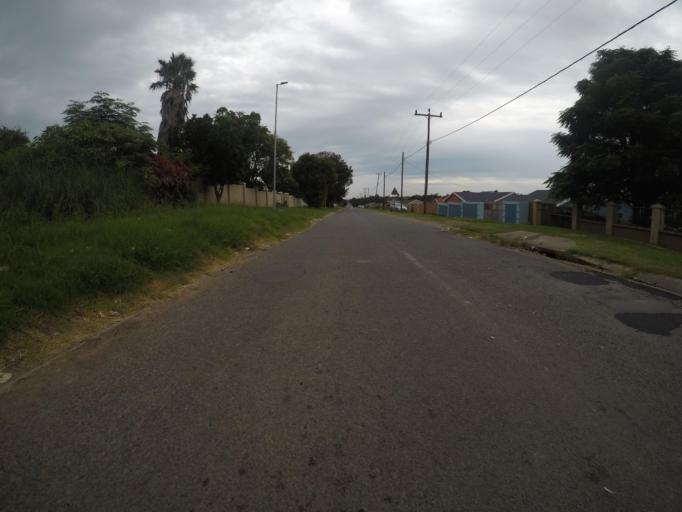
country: ZA
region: Eastern Cape
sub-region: Buffalo City Metropolitan Municipality
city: East London
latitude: -32.9929
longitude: 27.8474
